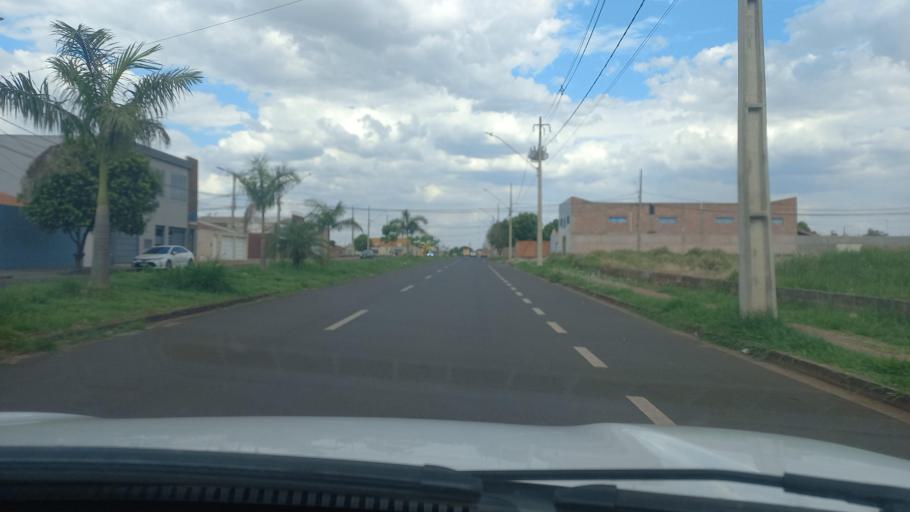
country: BR
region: Minas Gerais
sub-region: Uberaba
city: Uberaba
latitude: -19.7580
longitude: -47.9933
